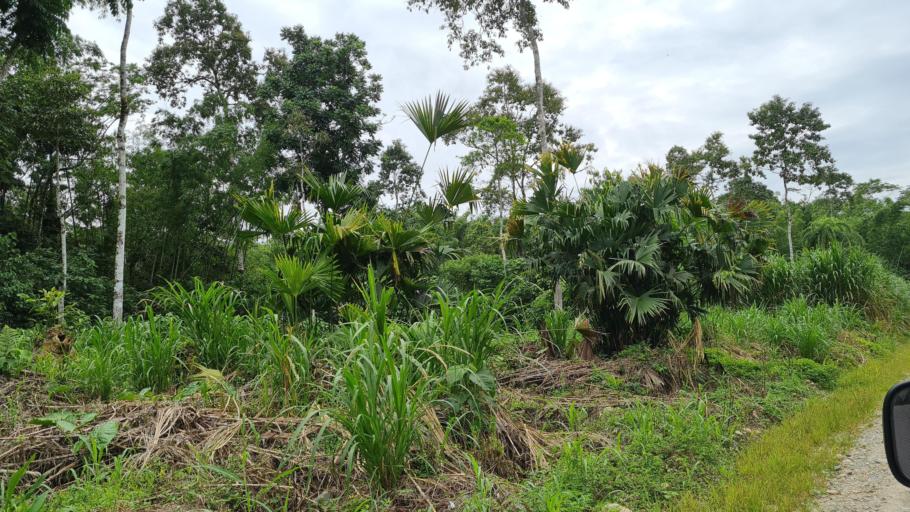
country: EC
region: Napo
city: Tena
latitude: -0.9932
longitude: -77.7475
